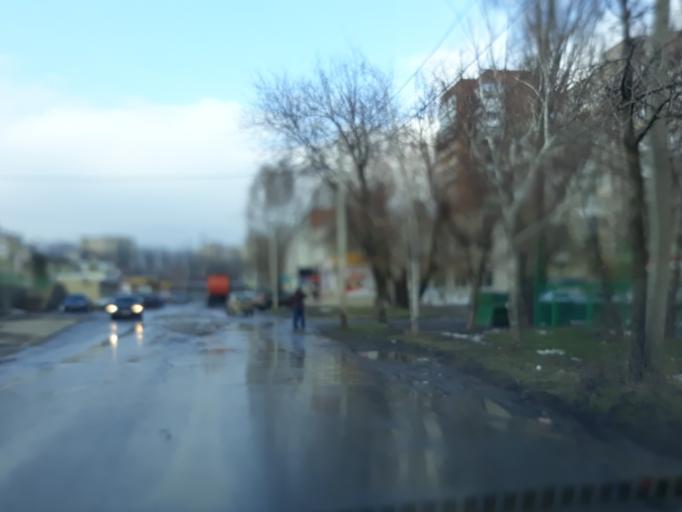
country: RU
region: Rostov
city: Taganrog
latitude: 47.2584
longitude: 38.9121
